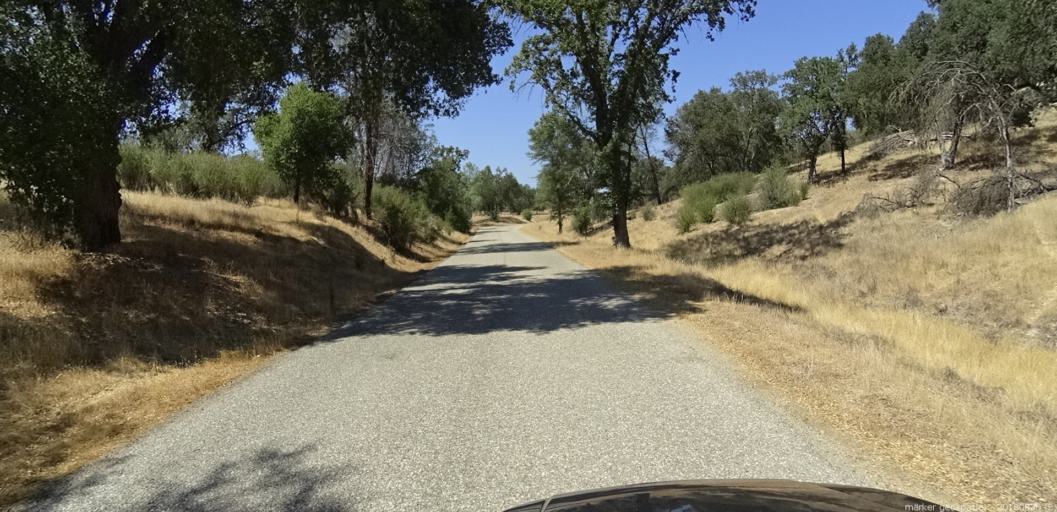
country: US
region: California
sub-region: Monterey County
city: King City
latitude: 35.9891
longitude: -121.2615
